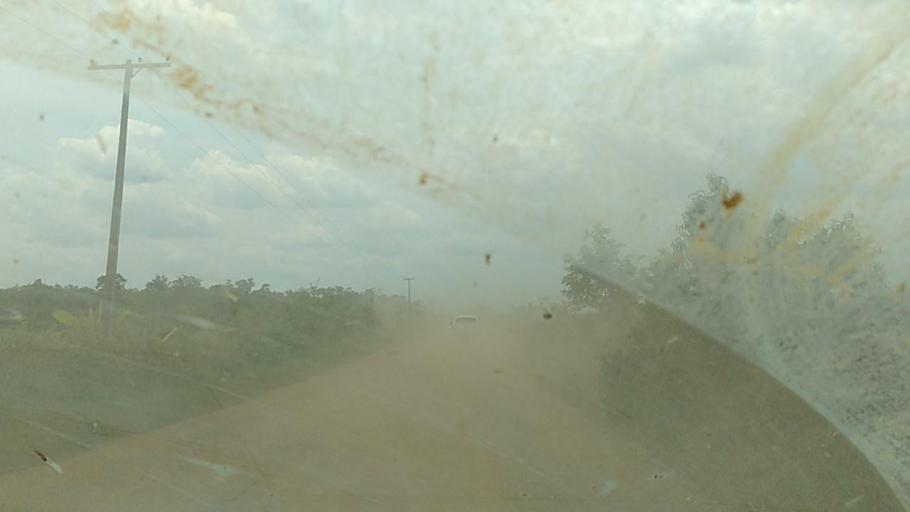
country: BR
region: Rondonia
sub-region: Porto Velho
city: Porto Velho
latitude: -8.9491
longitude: -64.3137
